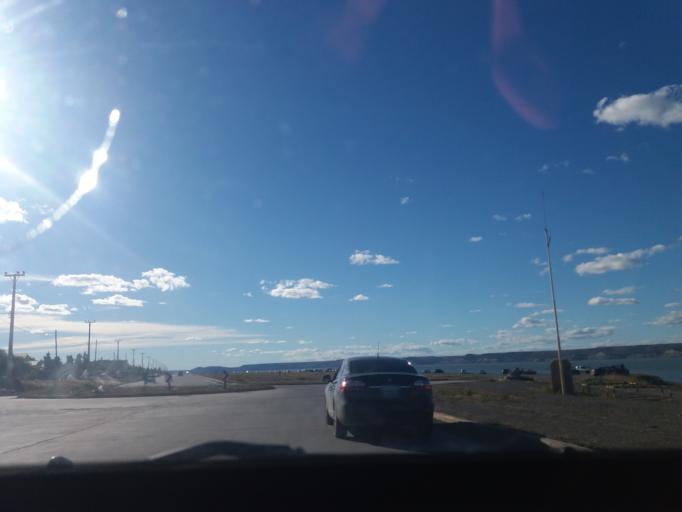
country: AR
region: Santa Cruz
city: Rio Gallegos
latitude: -51.6031
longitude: -69.2490
